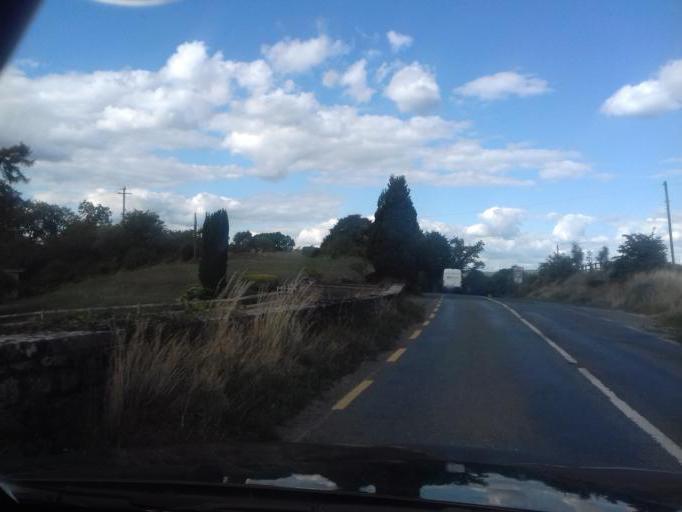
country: IE
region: Leinster
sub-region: Kilkenny
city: Thomastown
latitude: 52.5188
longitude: -7.1430
